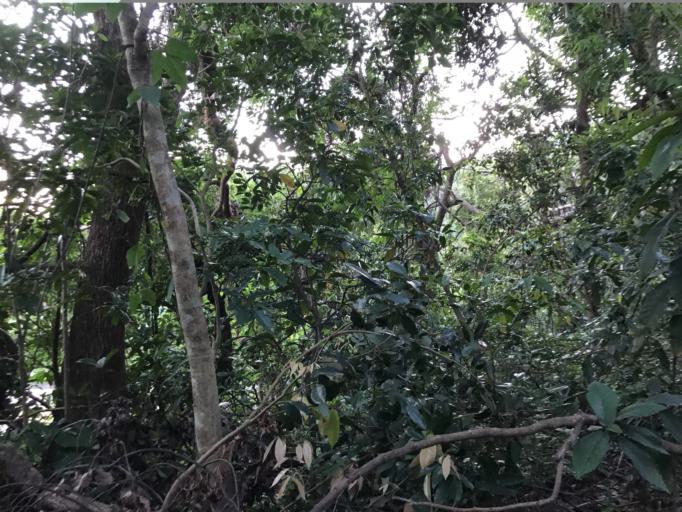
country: HK
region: Tai Po
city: Tai Po
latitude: 22.4699
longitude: 114.1467
